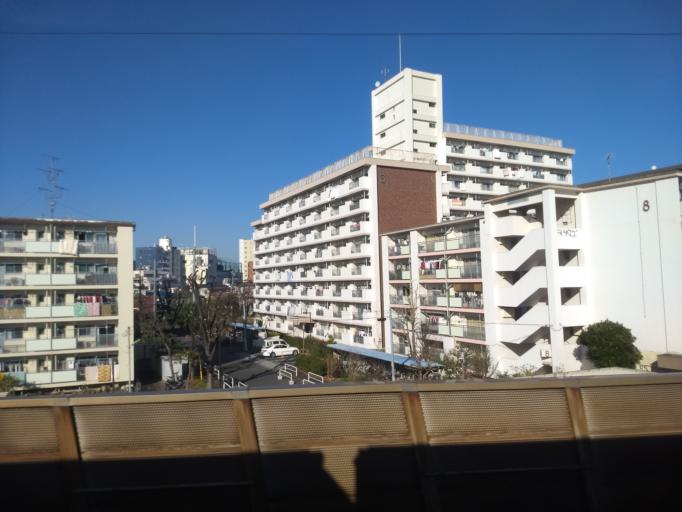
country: JP
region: Chiba
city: Matsudo
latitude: 35.7464
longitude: 139.8476
